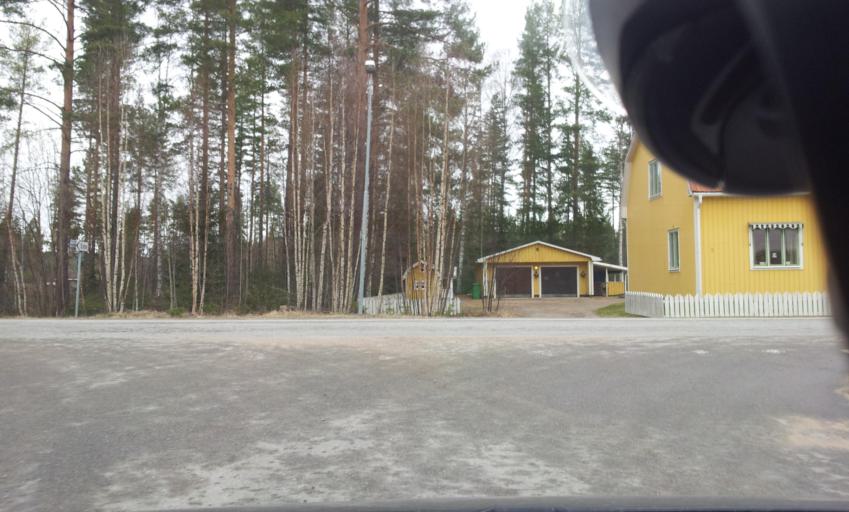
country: SE
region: Gaevleborg
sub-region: Ljusdals Kommun
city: Farila
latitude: 61.8006
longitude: 15.8971
